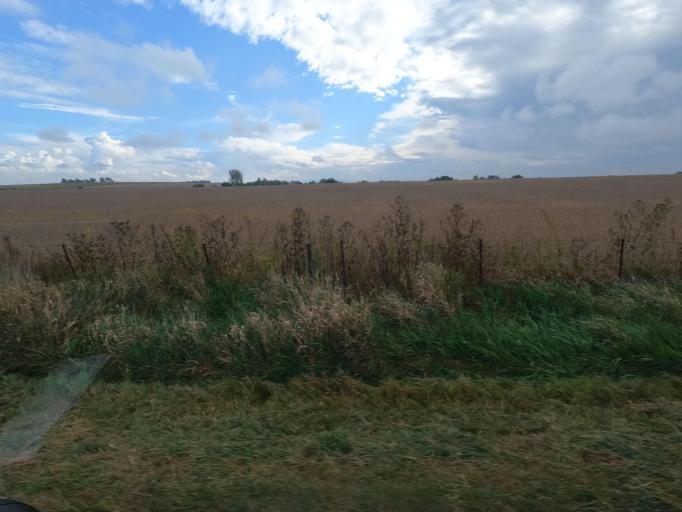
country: US
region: Iowa
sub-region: Henry County
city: Mount Pleasant
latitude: 40.7845
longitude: -91.5743
